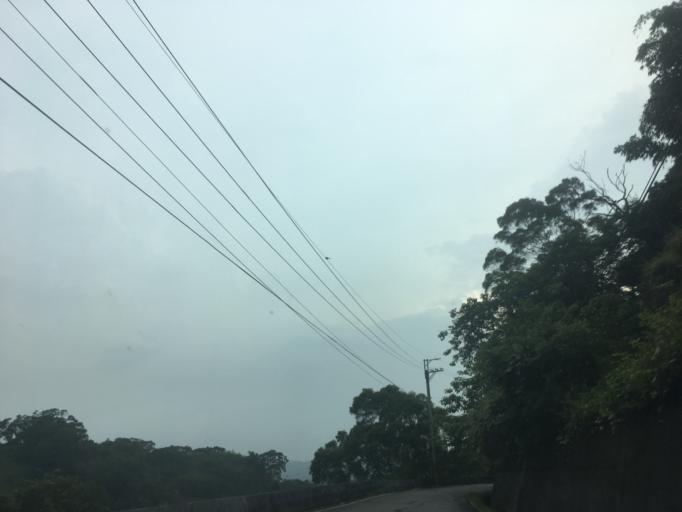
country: TW
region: Taiwan
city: Fengyuan
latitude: 24.1898
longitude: 120.7778
